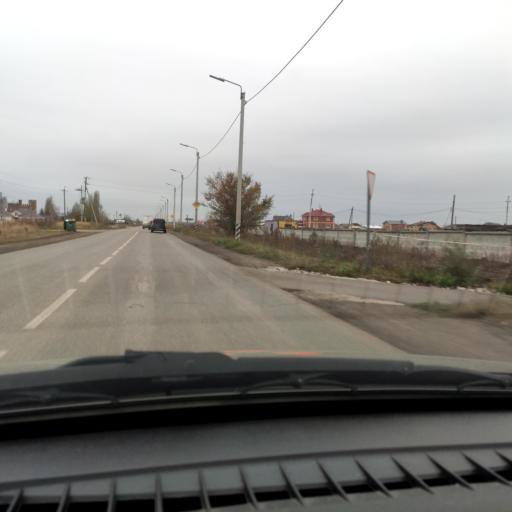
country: RU
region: Samara
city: Podstepki
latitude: 53.5223
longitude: 49.1701
